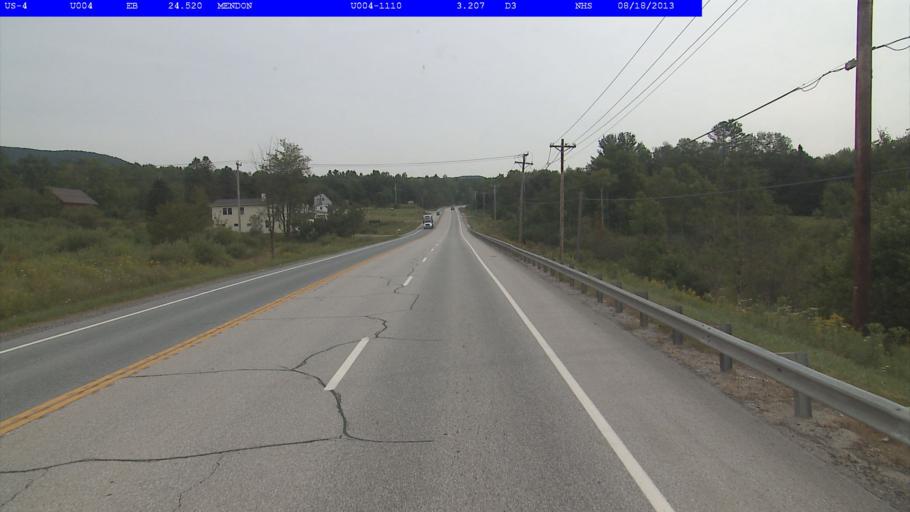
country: US
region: Vermont
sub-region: Rutland County
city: Rutland
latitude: 43.6524
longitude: -72.8921
